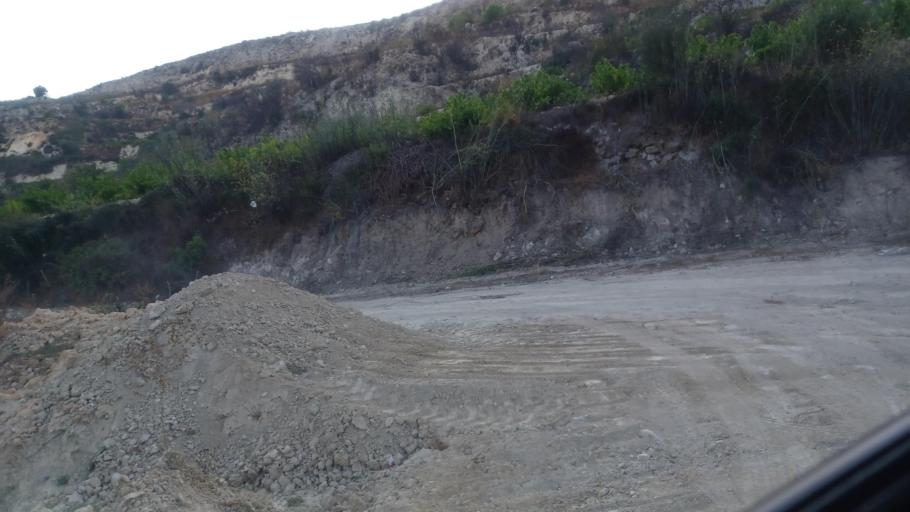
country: CY
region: Pafos
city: Tala
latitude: 34.8551
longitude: 32.4682
